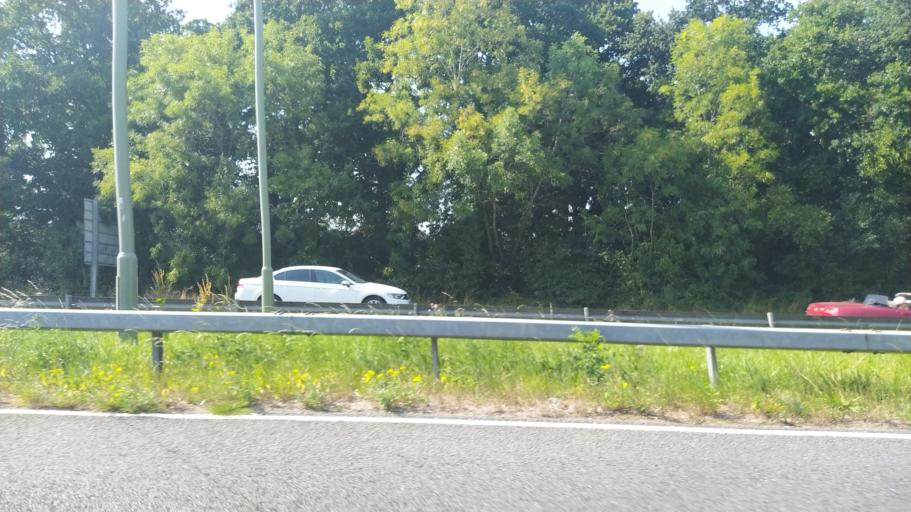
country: GB
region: England
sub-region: Hampshire
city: Totton
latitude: 50.9109
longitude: -1.4945
